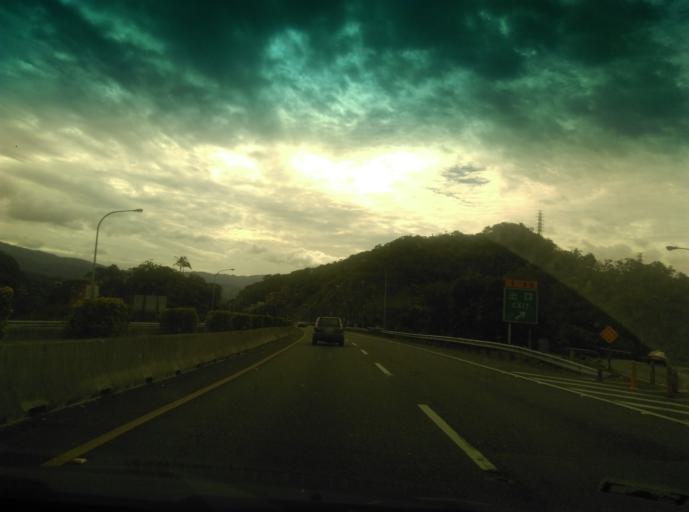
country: TW
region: Taiwan
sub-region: Keelung
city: Keelung
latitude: 25.1166
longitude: 121.7294
